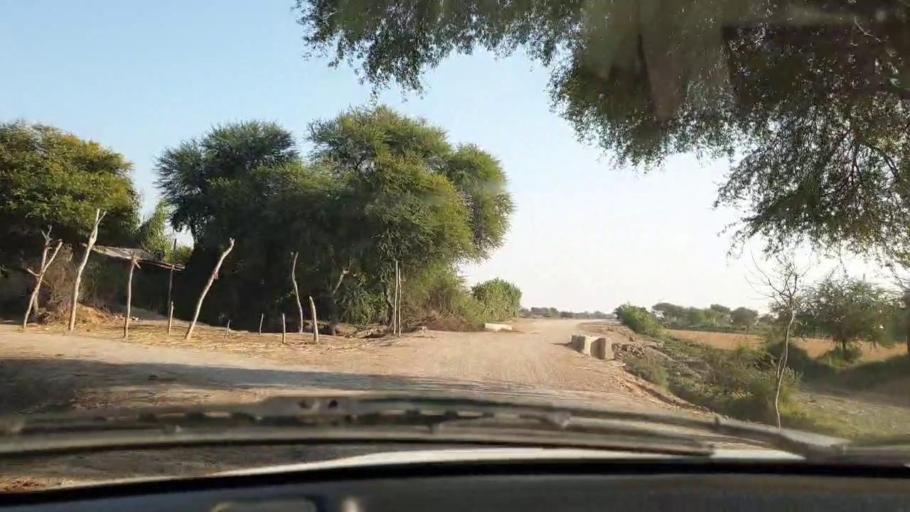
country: PK
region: Sindh
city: Bulri
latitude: 24.8024
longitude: 68.3924
